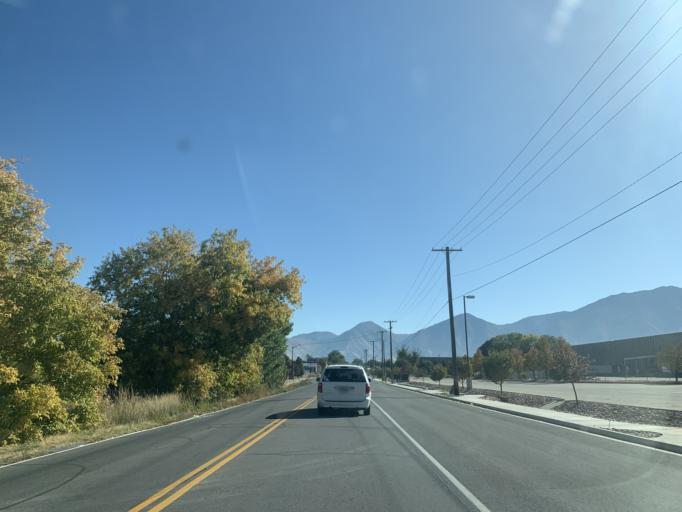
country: US
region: Utah
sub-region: Utah County
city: Payson
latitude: 40.0437
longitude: -111.7531
